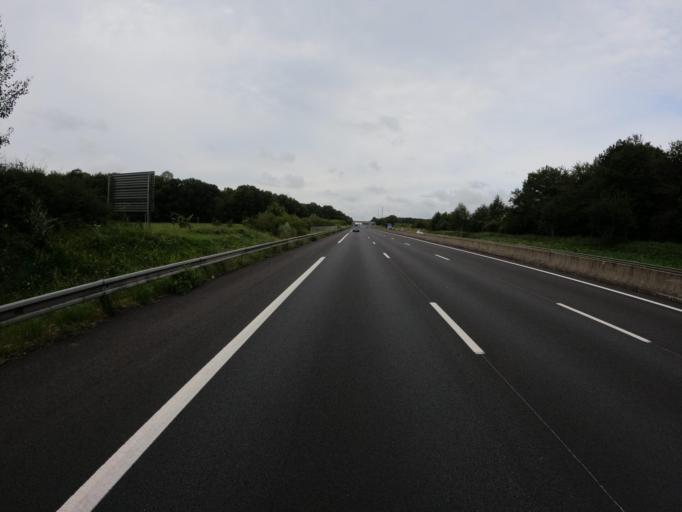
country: FR
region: Centre
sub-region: Departement d'Indre-et-Loire
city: Auzouer-en-Touraine
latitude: 47.5398
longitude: 0.9713
